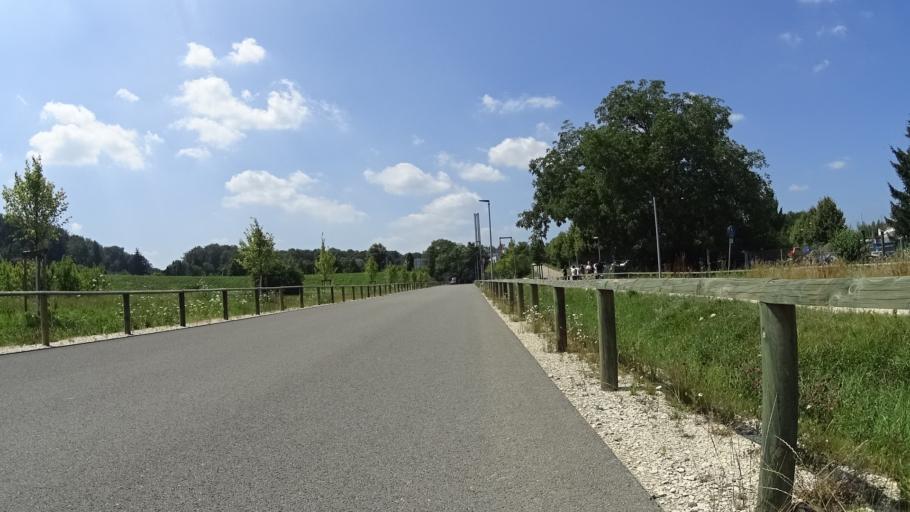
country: DE
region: Baden-Wuerttemberg
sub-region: Regierungsbezirk Stuttgart
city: Goeppingen
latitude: 48.7019
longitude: 9.6377
